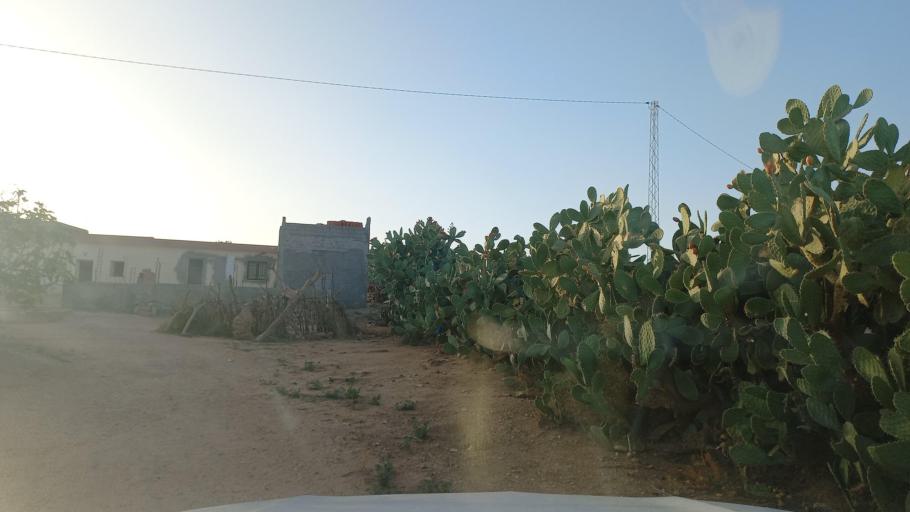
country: TN
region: Al Qasrayn
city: Sbiba
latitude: 35.3740
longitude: 9.0073
